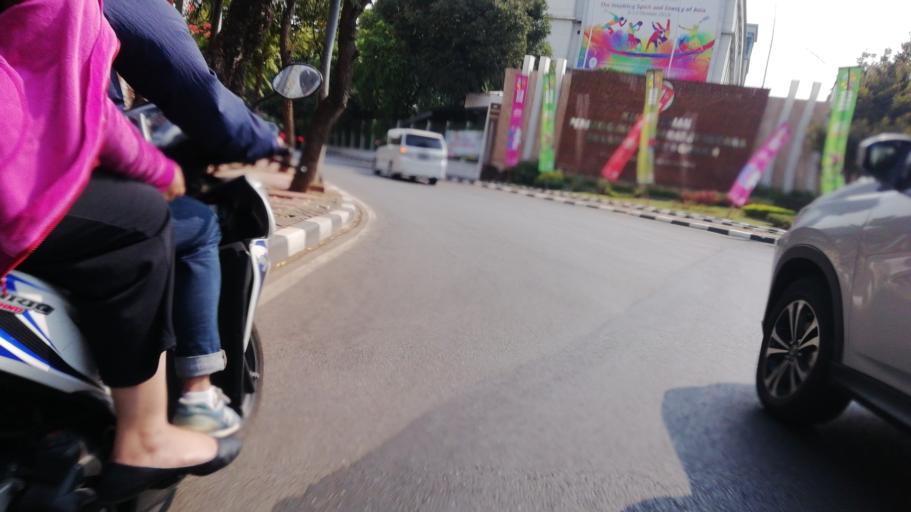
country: ID
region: Jakarta Raya
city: Jakarta
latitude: -6.2281
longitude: 106.8012
